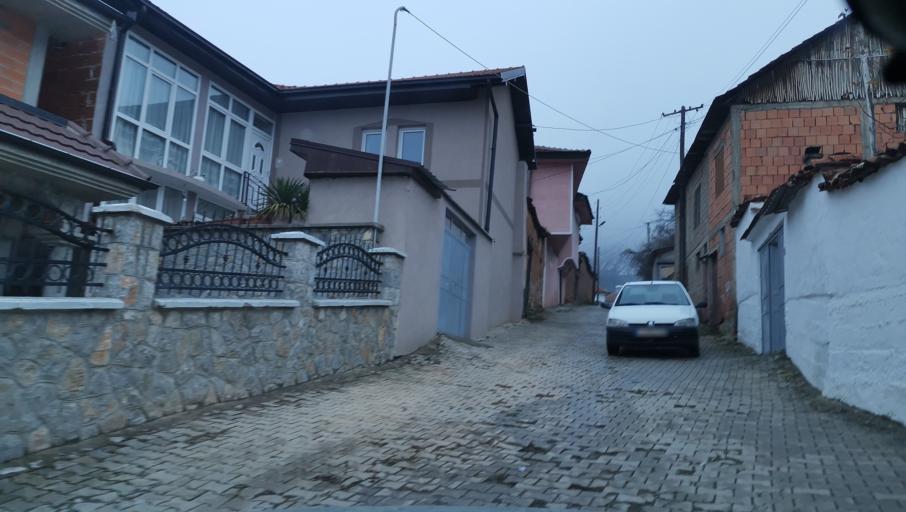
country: MK
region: Debar
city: Debar
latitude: 41.5269
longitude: 20.5282
